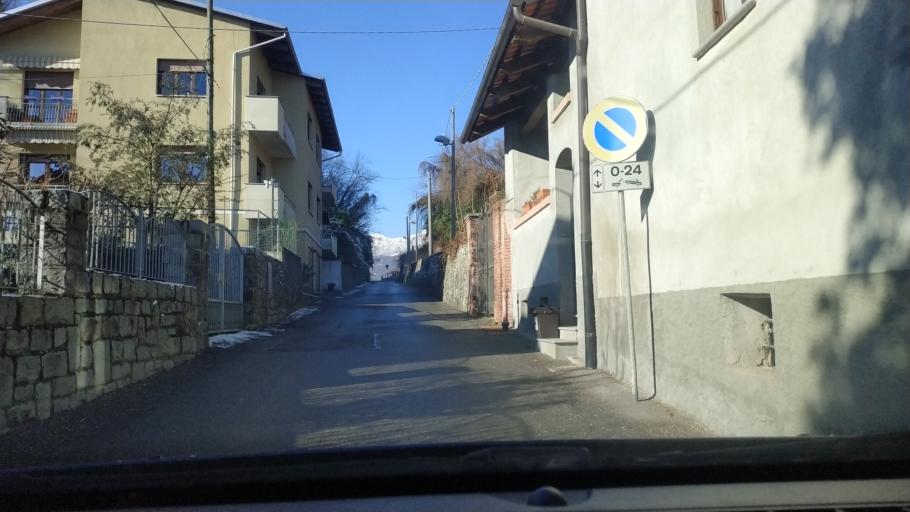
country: IT
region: Piedmont
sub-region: Provincia di Torino
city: Salerano Canavese
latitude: 45.4572
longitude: 7.8495
